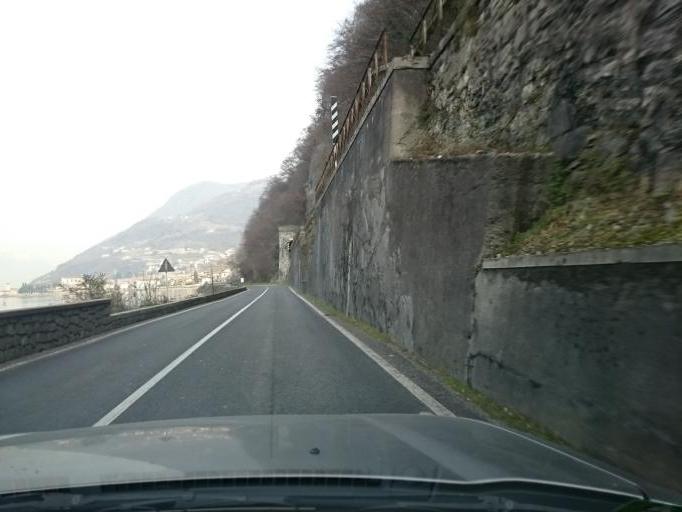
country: IT
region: Lombardy
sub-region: Provincia di Brescia
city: Pisogne
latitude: 45.7920
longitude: 10.0967
